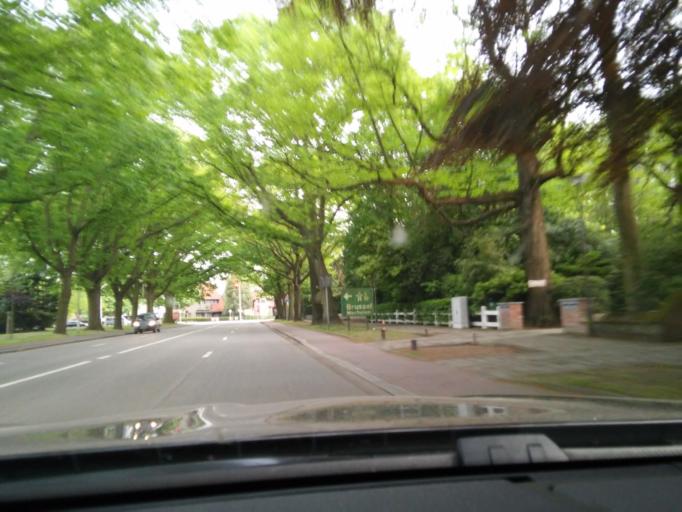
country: BE
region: Flanders
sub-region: Provincie Antwerpen
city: Edegem
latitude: 51.1771
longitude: 4.4114
